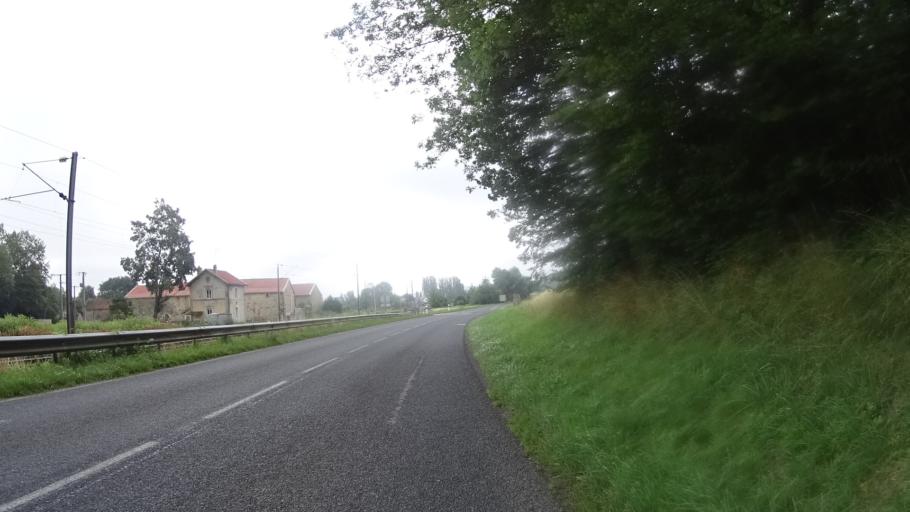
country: FR
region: Lorraine
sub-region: Departement de la Meuse
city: Fains-Veel
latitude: 48.8027
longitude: 5.1089
